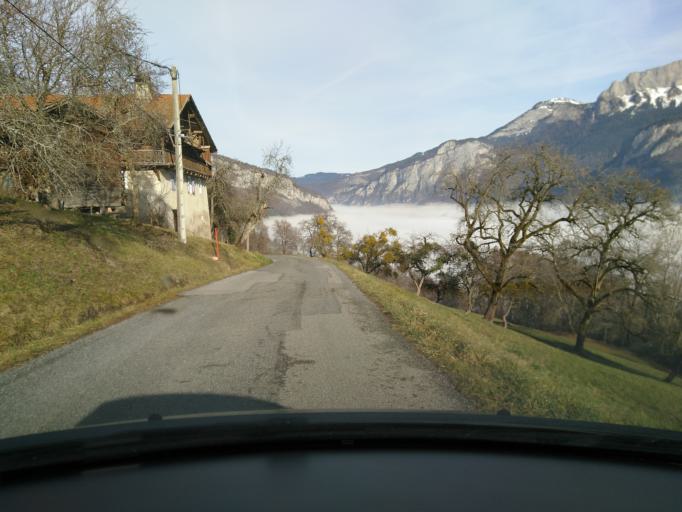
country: FR
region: Rhone-Alpes
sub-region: Departement de la Haute-Savoie
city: Sallanches
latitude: 45.9586
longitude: 6.6129
